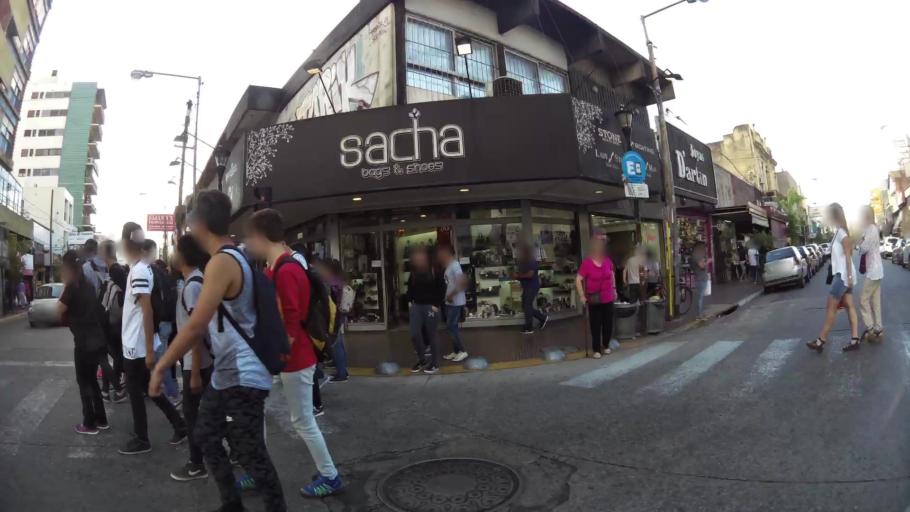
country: AR
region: Buenos Aires
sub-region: Partido de General San Martin
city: General San Martin
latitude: -34.5503
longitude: -58.5549
